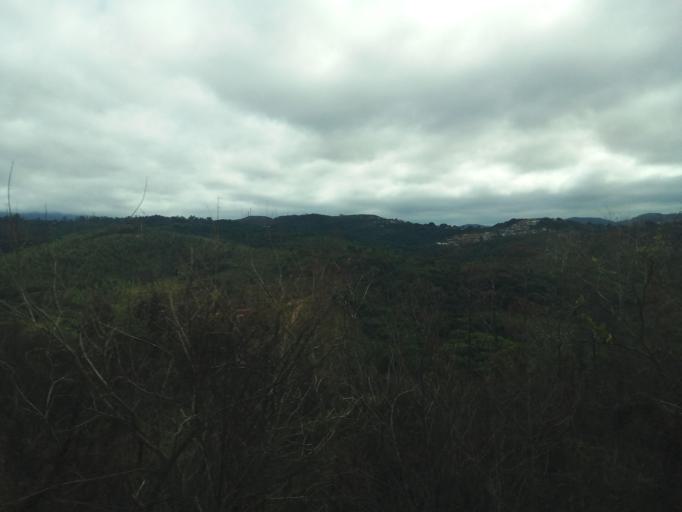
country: BR
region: Minas Gerais
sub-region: Caete
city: Caete
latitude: -19.9096
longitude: -43.6924
